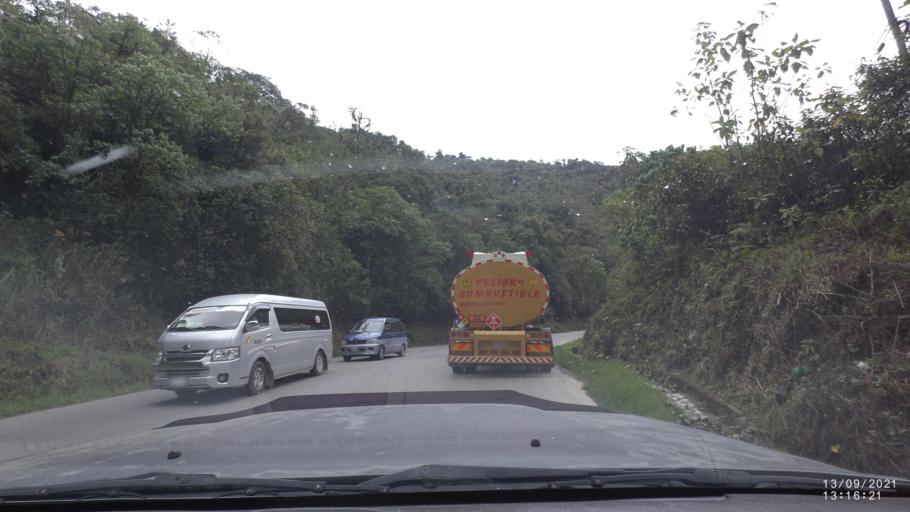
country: BO
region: Cochabamba
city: Colomi
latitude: -17.2038
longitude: -65.8572
